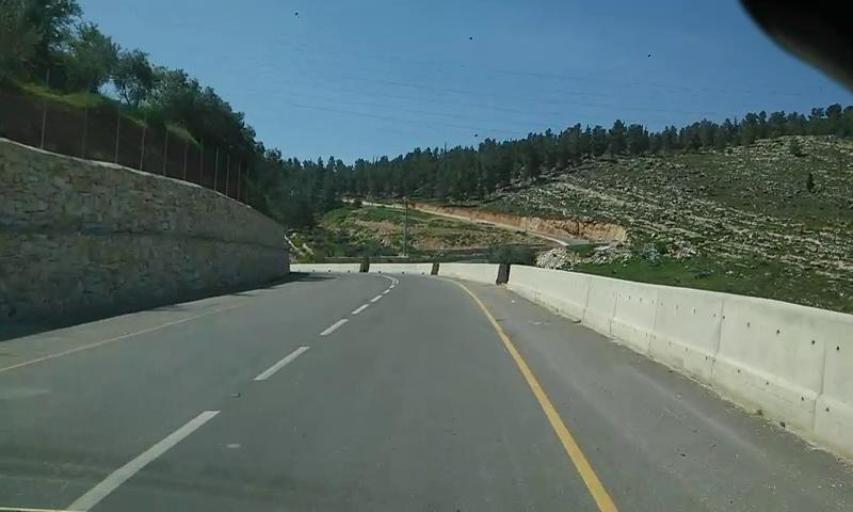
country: PS
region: West Bank
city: Nahhalin
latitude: 31.6790
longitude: 35.1108
